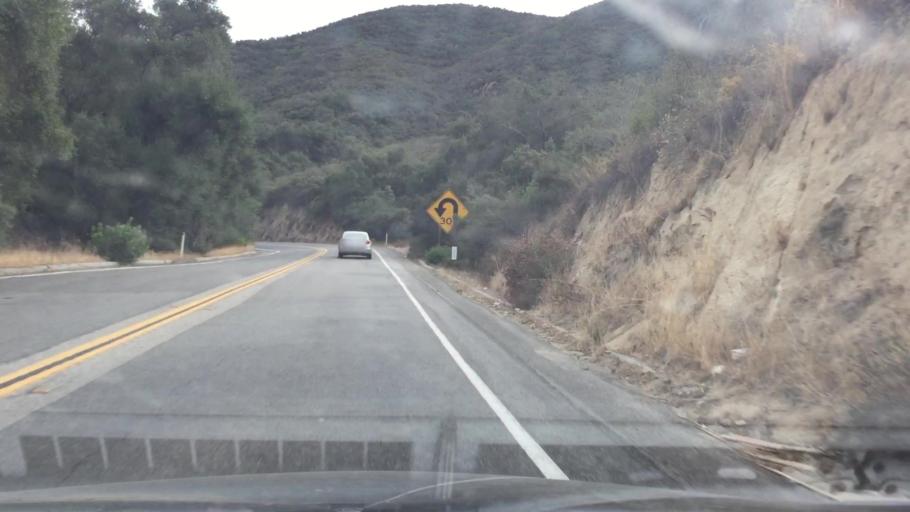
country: US
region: California
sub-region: Riverside County
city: Lakeland Village
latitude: 33.6069
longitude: -117.4334
